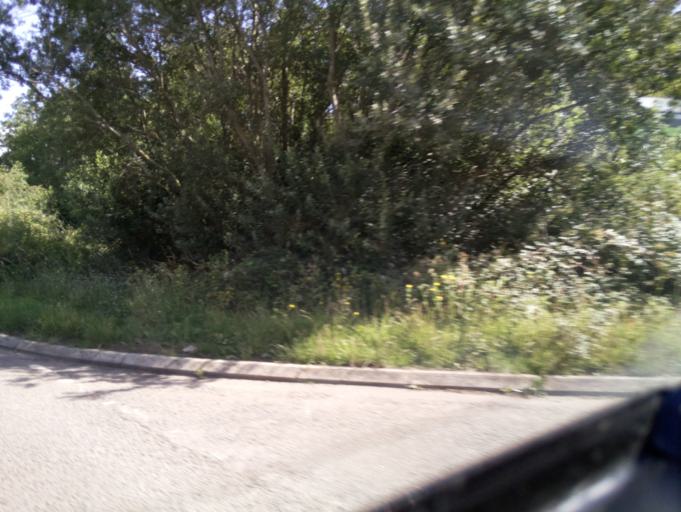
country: GB
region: England
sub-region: Buckinghamshire
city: Winslow
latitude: 51.9845
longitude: -0.8538
